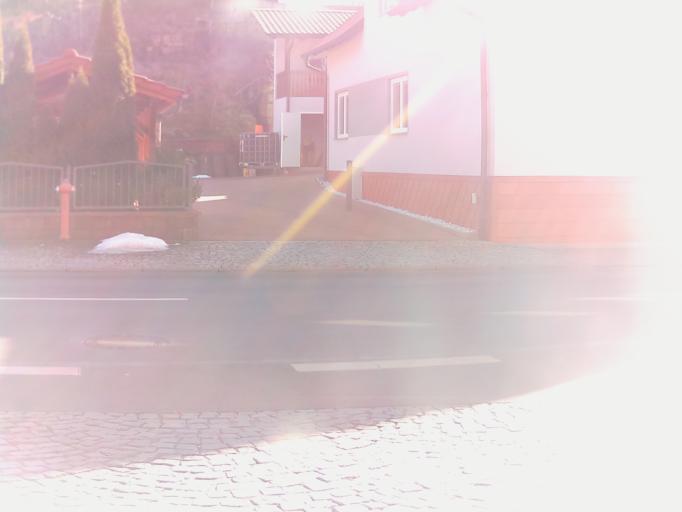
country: DE
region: Thuringia
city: Belrieth
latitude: 50.5279
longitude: 10.4965
